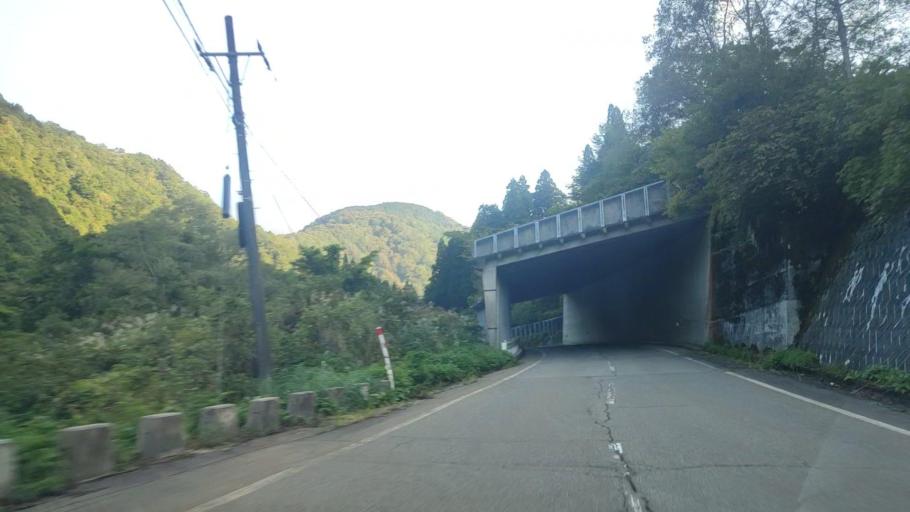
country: JP
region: Toyama
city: Yatsuomachi-higashikumisaka
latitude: 36.4913
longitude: 137.0490
